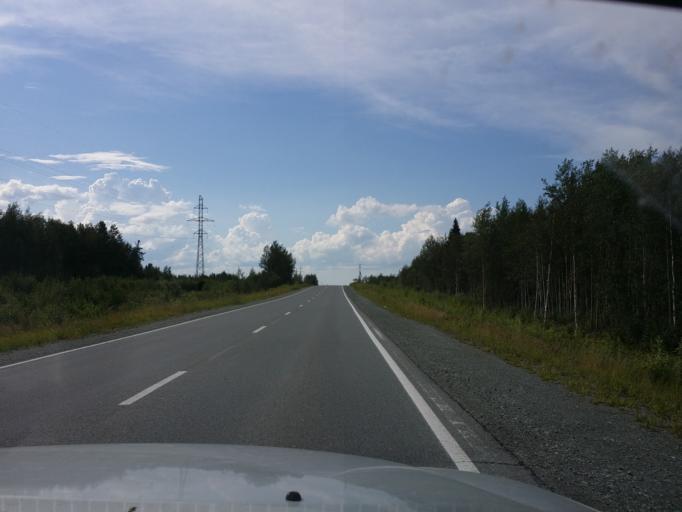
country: RU
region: Khanty-Mansiyskiy Avtonomnyy Okrug
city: Megion
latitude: 61.1025
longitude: 75.9537
